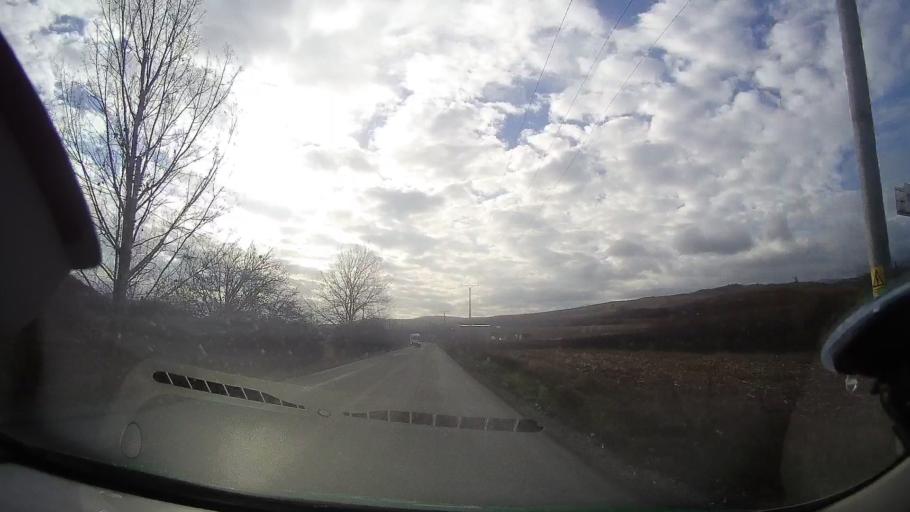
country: RO
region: Cluj
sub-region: Comuna Floresti
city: Luna de Sus
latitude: 46.7254
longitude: 23.4197
